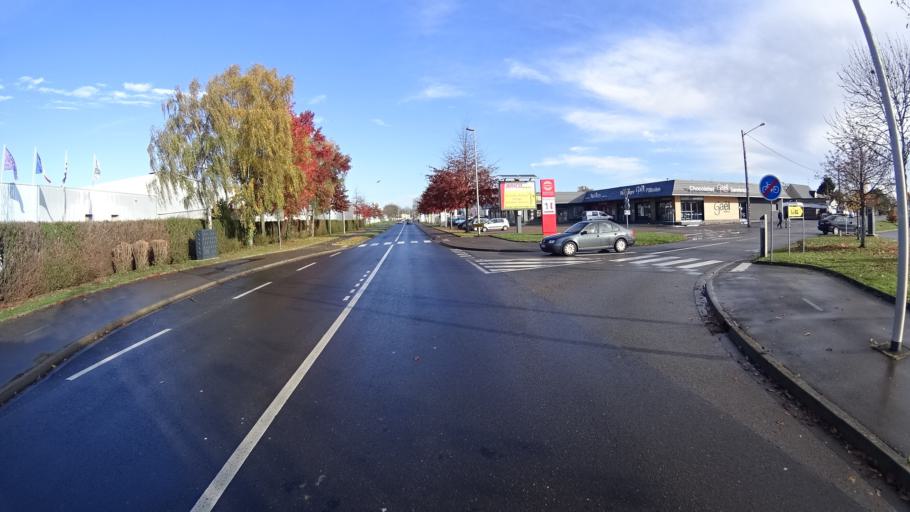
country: FR
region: Brittany
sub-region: Departement d'Ille-et-Vilaine
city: Redon
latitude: 47.6670
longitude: -2.0699
